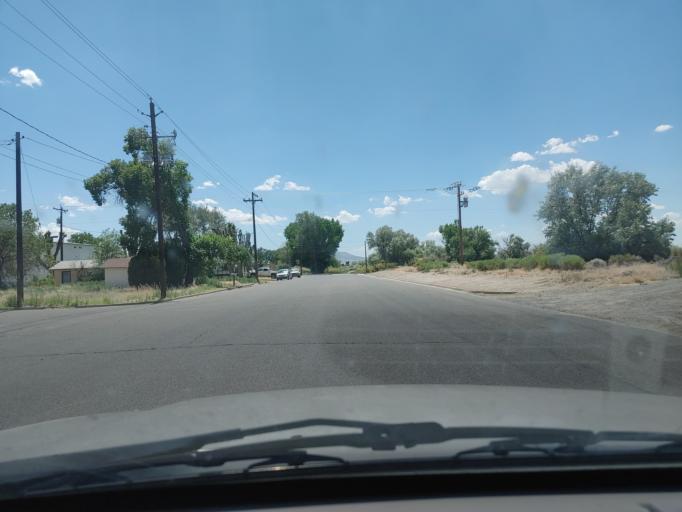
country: US
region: Nevada
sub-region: Humboldt County
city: Winnemucca
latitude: 40.9701
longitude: -117.7411
